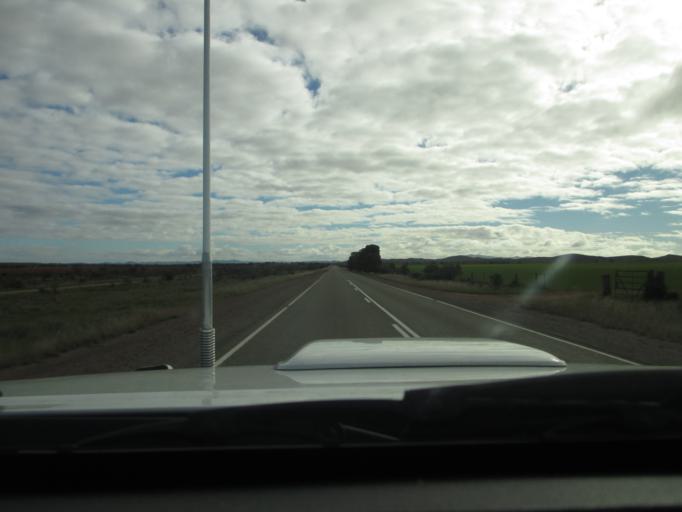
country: AU
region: South Australia
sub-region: Flinders Ranges
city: Quorn
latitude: -32.4477
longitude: 138.5363
